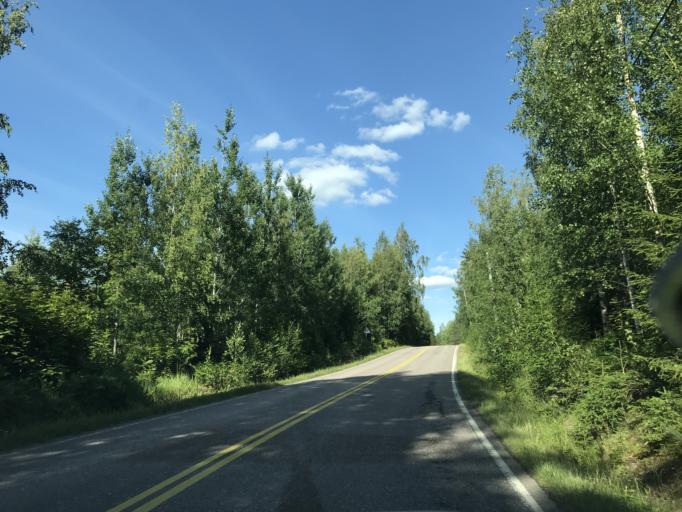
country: FI
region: Uusimaa
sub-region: Helsinki
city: Vihti
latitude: 60.4360
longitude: 24.5412
